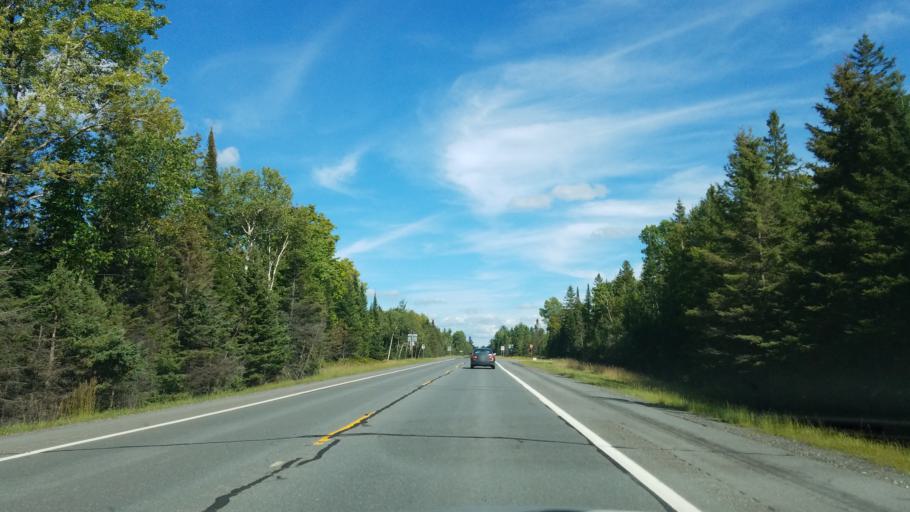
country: US
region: Michigan
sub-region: Baraga County
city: L'Anse
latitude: 46.5788
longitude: -88.3986
